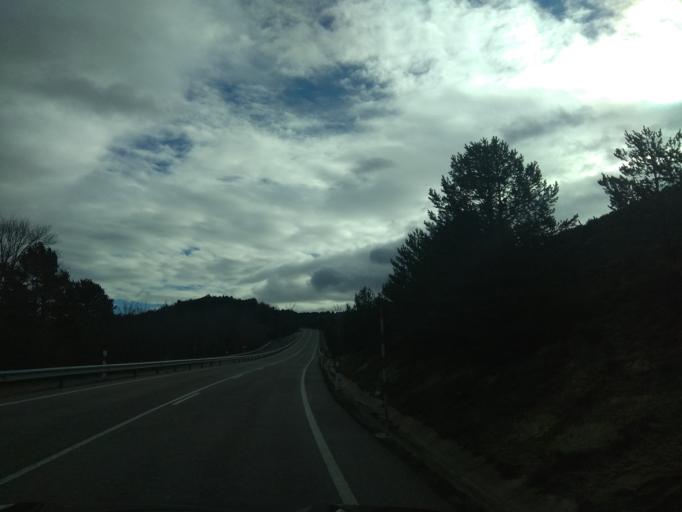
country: ES
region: Castille and Leon
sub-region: Provincia de Burgos
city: Arija
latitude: 42.9984
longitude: -3.8381
